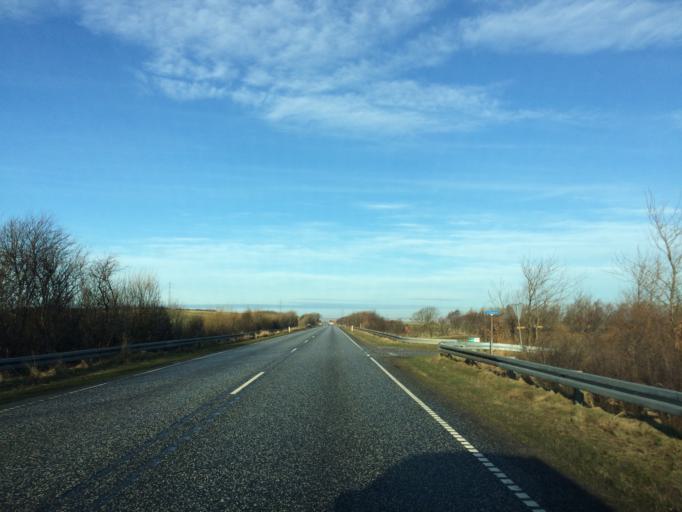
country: DK
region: Central Jutland
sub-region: Struer Kommune
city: Struer
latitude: 56.5479
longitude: 8.5593
